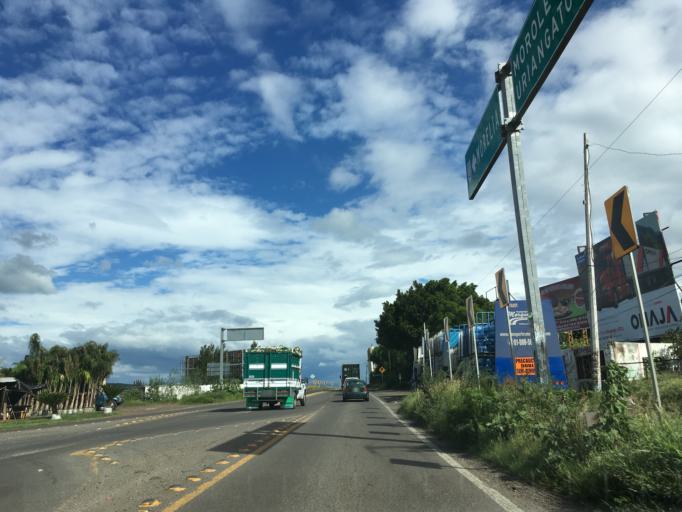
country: MX
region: Guanajuato
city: Moroleon
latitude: 20.1012
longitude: -101.1620
